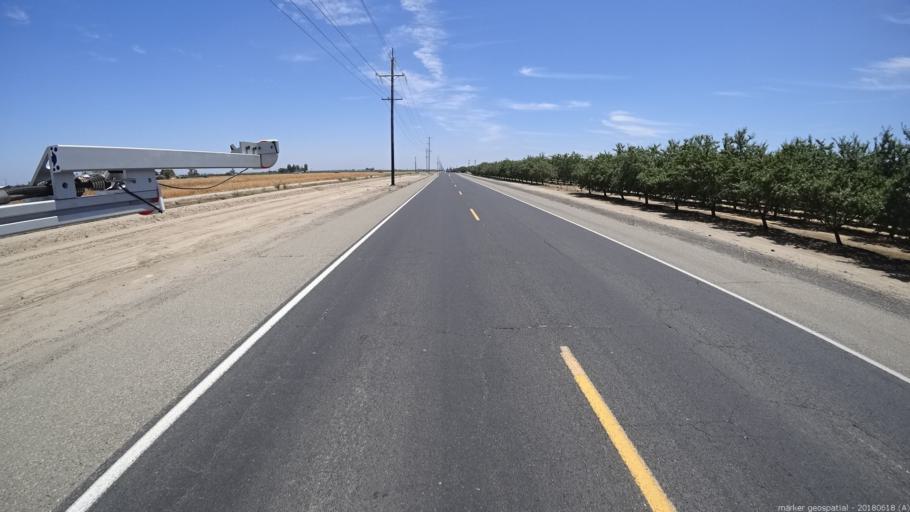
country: US
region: California
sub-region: Madera County
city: Parkwood
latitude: 36.9238
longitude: -120.0950
